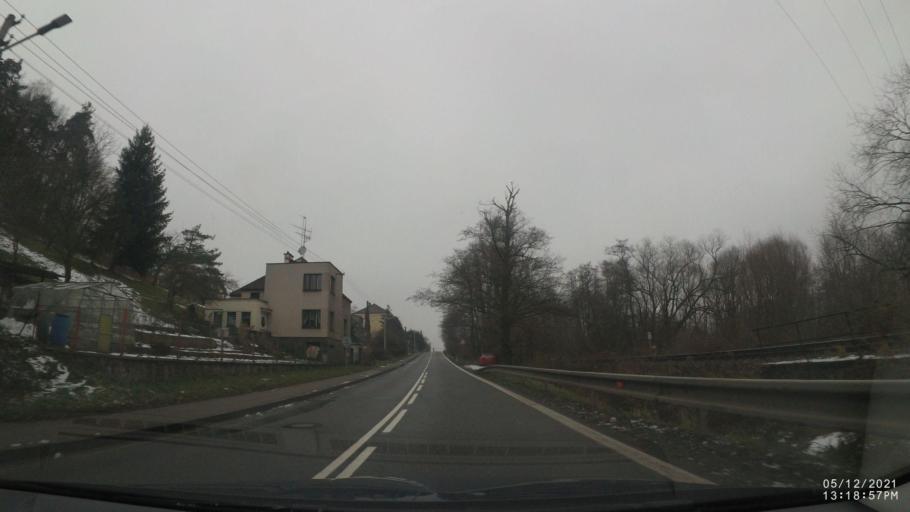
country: CZ
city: Velke Porici
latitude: 50.4388
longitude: 16.1931
